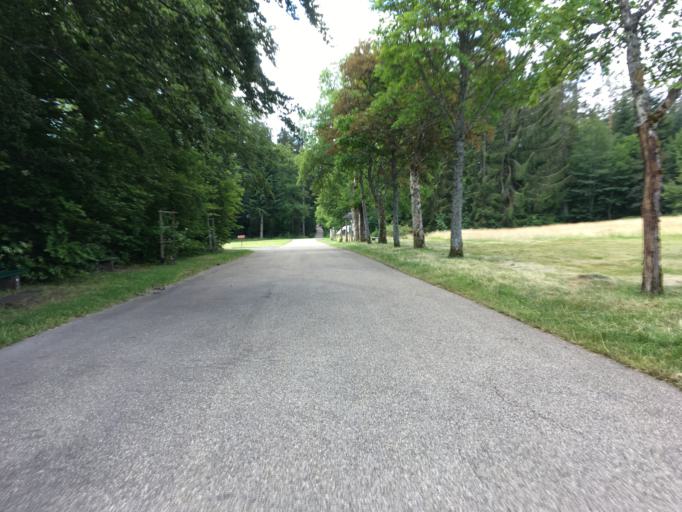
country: DE
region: Baden-Wuerttemberg
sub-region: Karlsruhe Region
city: Freudenstadt
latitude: 48.4525
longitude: 8.4094
